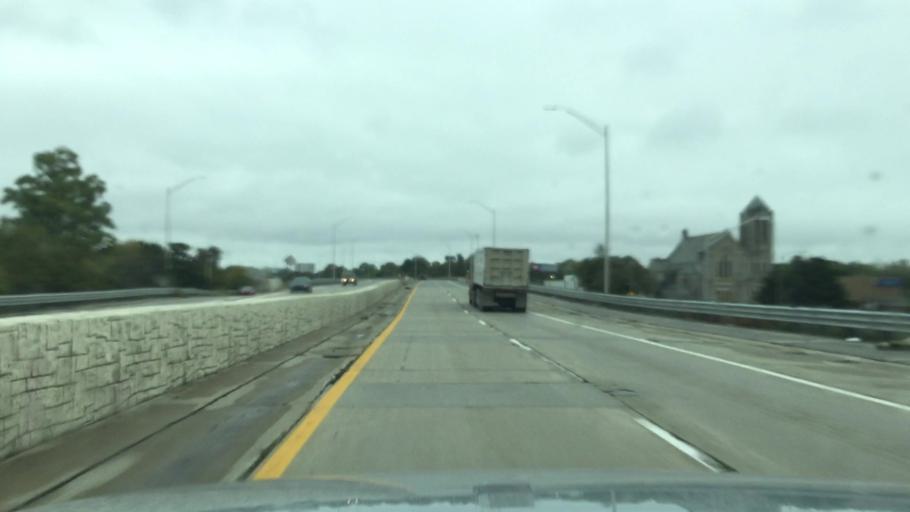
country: US
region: Michigan
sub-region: Saginaw County
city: Saginaw
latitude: 43.4368
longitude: -83.9363
